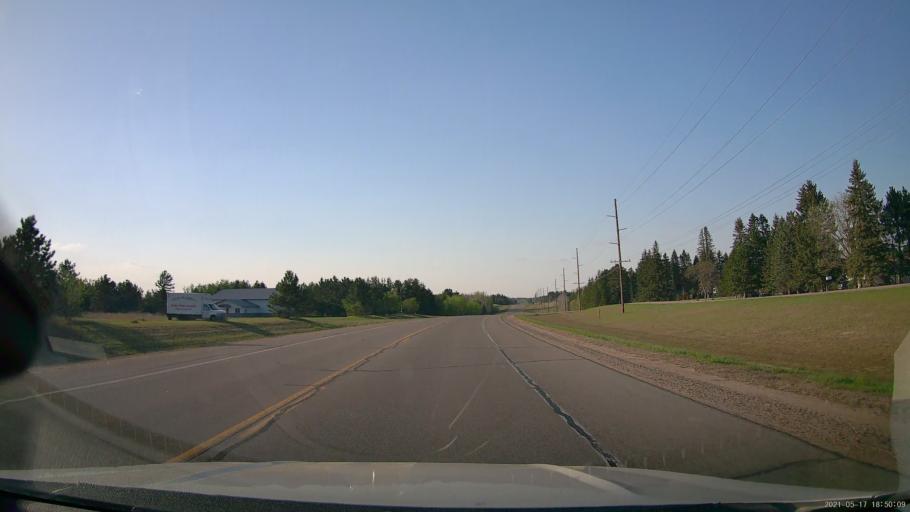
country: US
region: Minnesota
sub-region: Hubbard County
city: Park Rapids
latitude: 46.9298
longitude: -95.0167
